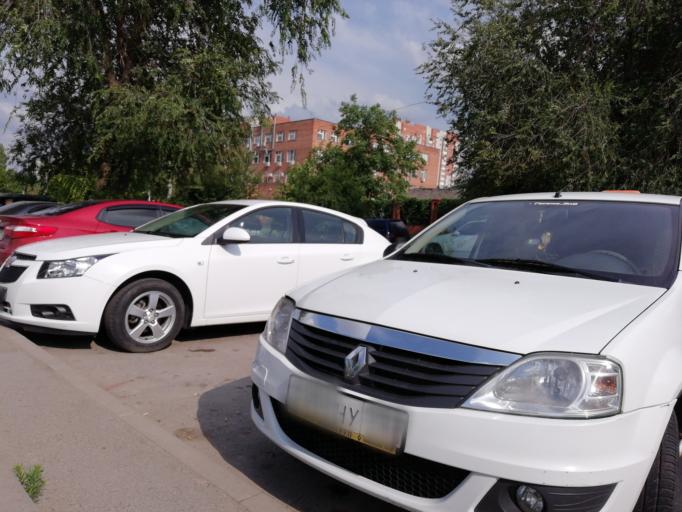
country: RU
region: Rostov
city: Severnyy
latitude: 47.2743
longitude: 39.7081
